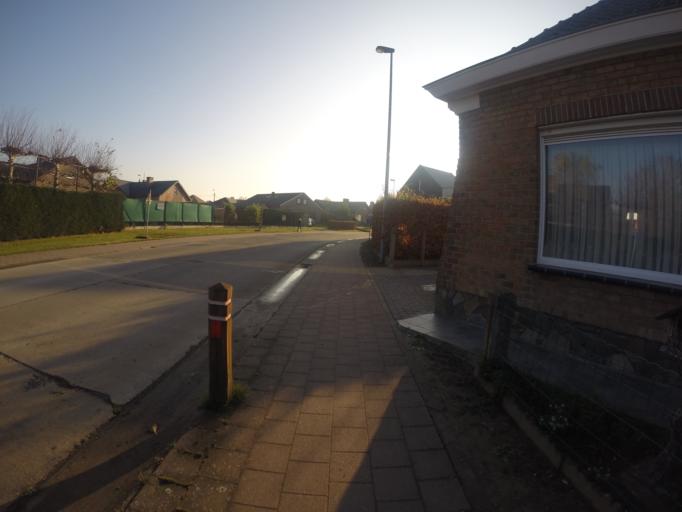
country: BE
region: Flanders
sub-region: Provincie Oost-Vlaanderen
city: Aalter
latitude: 51.0894
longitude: 3.4400
